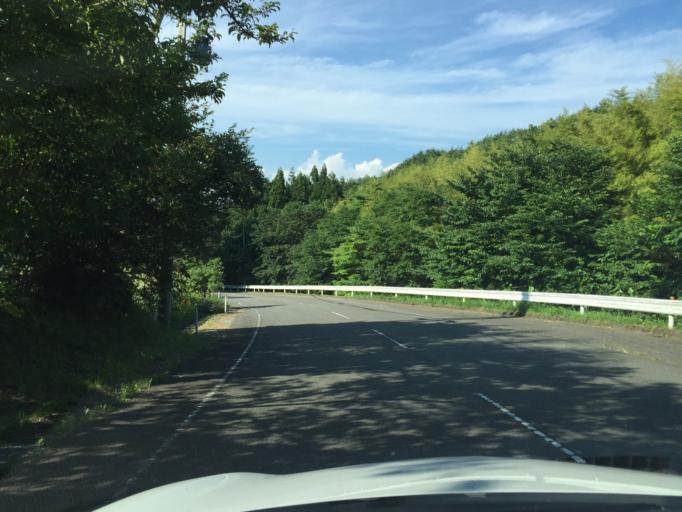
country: JP
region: Fukushima
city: Sukagawa
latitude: 37.2722
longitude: 140.5026
